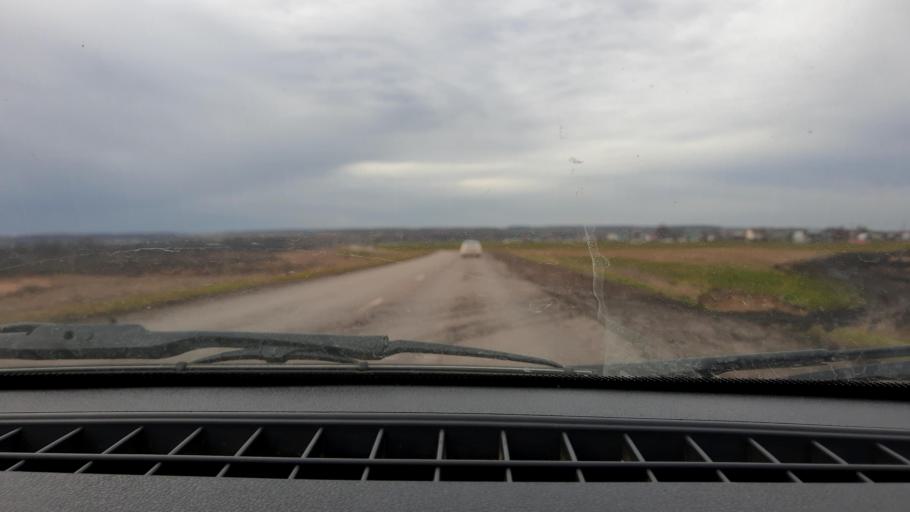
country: RU
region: Bashkortostan
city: Mikhaylovka
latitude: 54.8303
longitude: 55.9607
